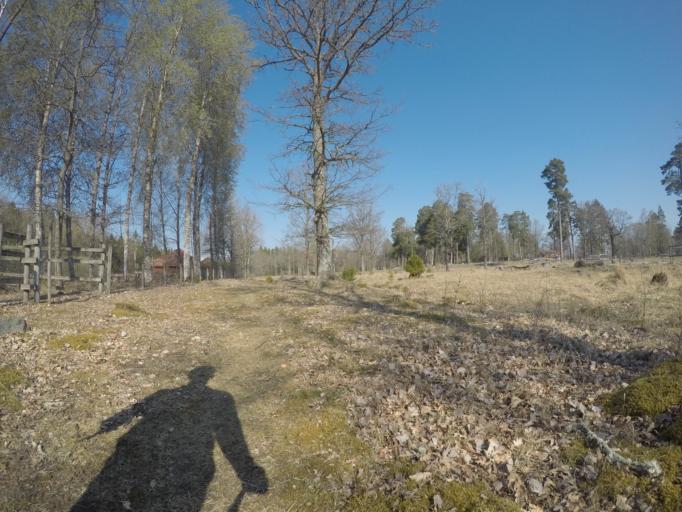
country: SE
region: Vaestmanland
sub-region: Hallstahammars Kommun
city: Kolback
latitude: 59.5323
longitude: 16.2828
